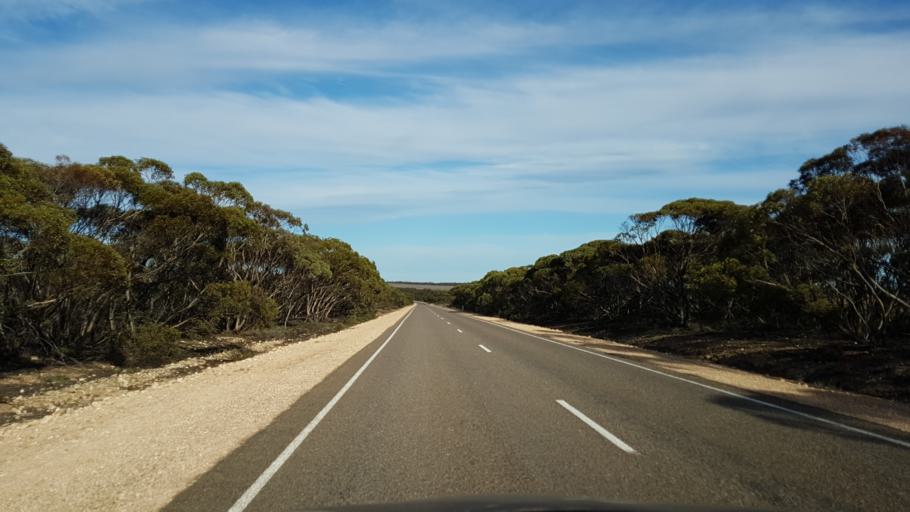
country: AU
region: South Australia
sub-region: Mid Murray
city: Mannum
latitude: -35.0312
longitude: 139.4875
